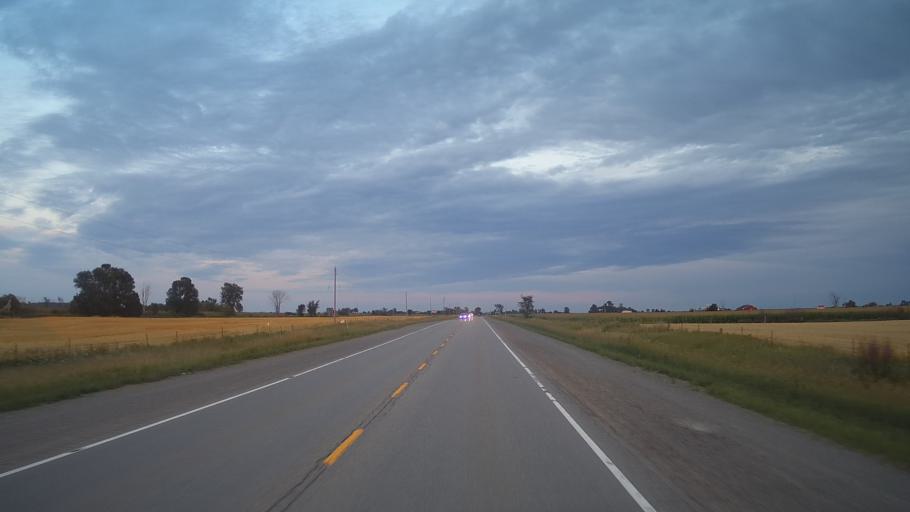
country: CA
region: Ontario
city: Pembroke
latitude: 45.6858
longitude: -76.9477
